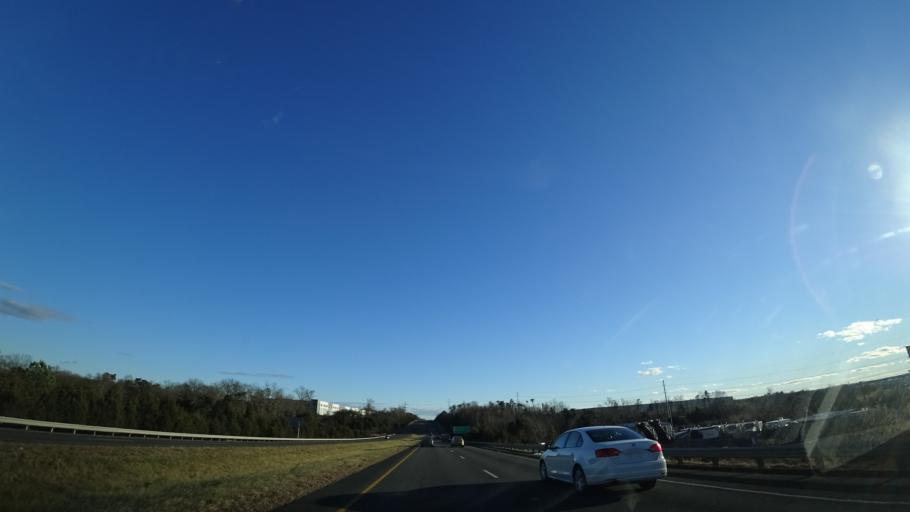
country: US
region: Virginia
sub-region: Prince William County
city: Bull Run
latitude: 38.7828
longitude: -77.5471
